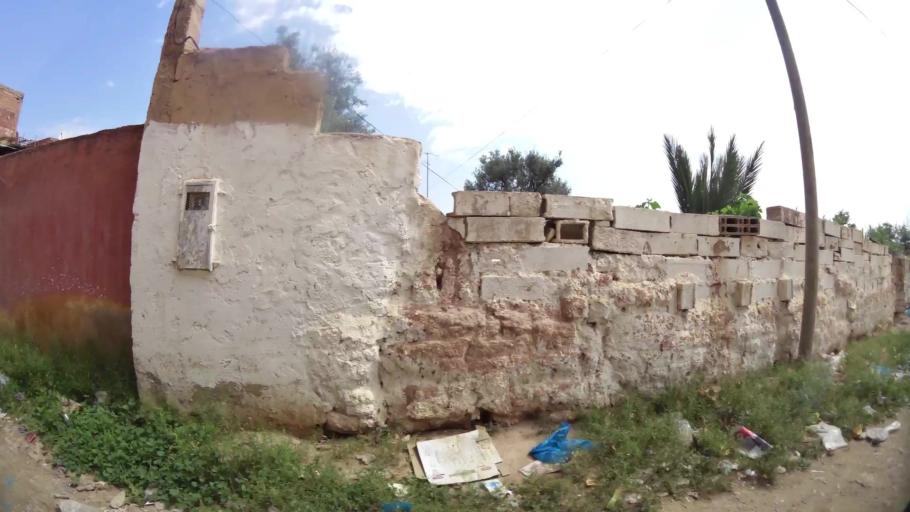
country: MA
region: Oriental
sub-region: Oujda-Angad
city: Oujda
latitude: 34.6814
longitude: -1.8963
